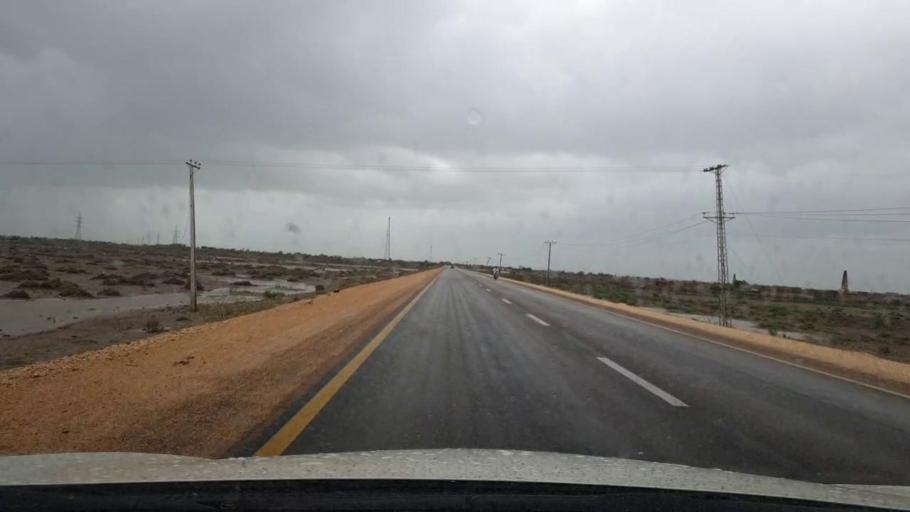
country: PK
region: Sindh
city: Kario
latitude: 24.6526
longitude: 68.6450
